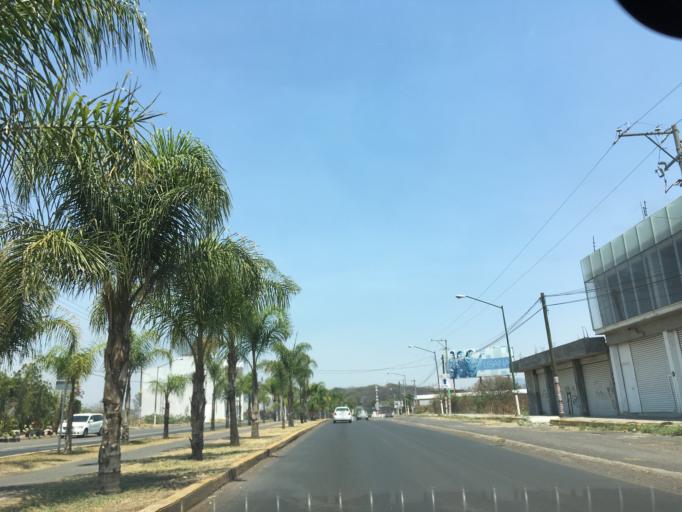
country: MX
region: Guanajuato
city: Moroleon
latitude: 20.1046
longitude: -101.1664
